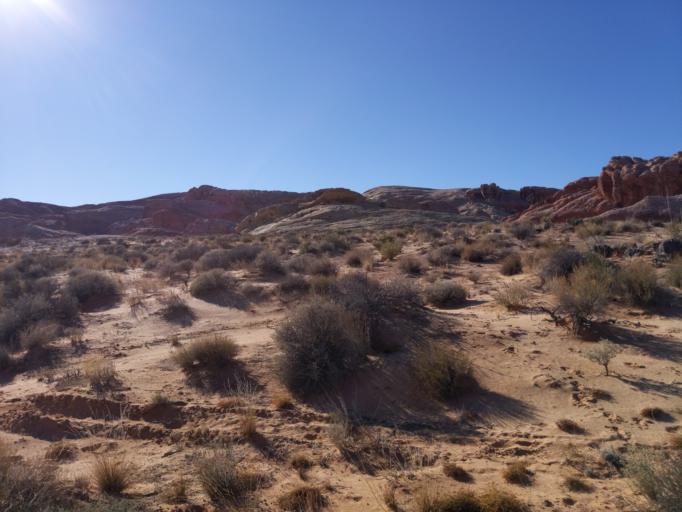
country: US
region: Nevada
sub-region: Clark County
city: Moapa Valley
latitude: 36.4707
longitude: -114.5257
